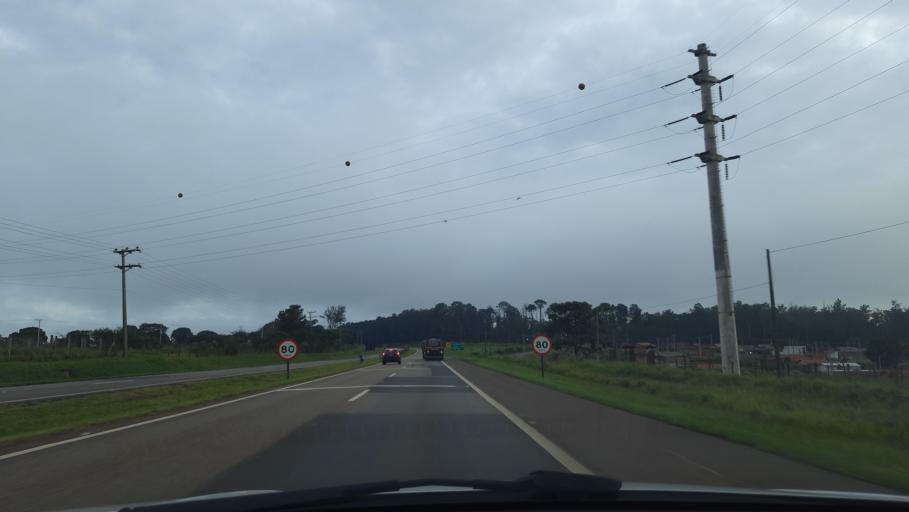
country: BR
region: Sao Paulo
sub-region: Casa Branca
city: Casa Branca
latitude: -21.7614
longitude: -47.0702
